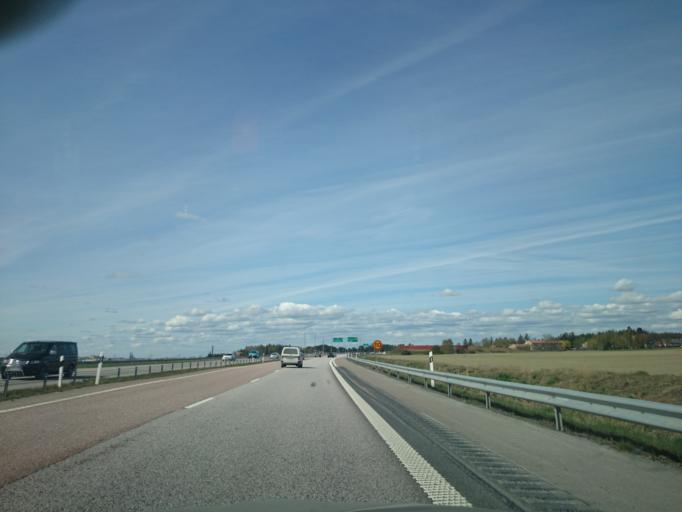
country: SE
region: Uppsala
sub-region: Uppsala Kommun
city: Saevja
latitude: 59.8264
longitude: 17.7422
